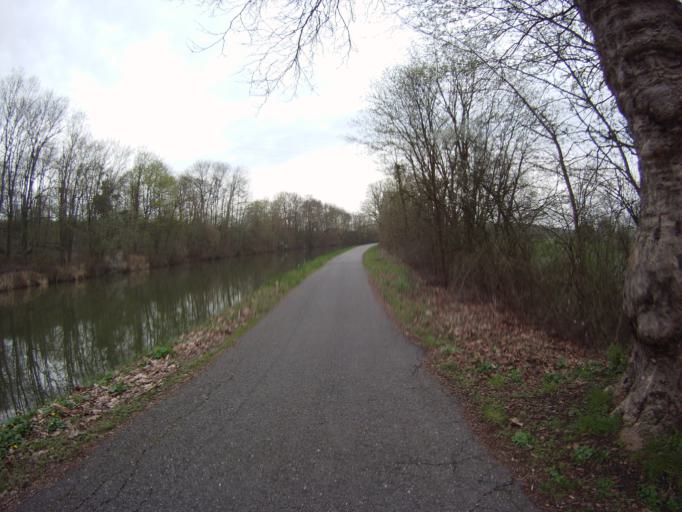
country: FR
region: Lorraine
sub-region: Departement de Meurthe-et-Moselle
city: Laneuveville-devant-Nancy
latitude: 48.6478
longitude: 6.2220
